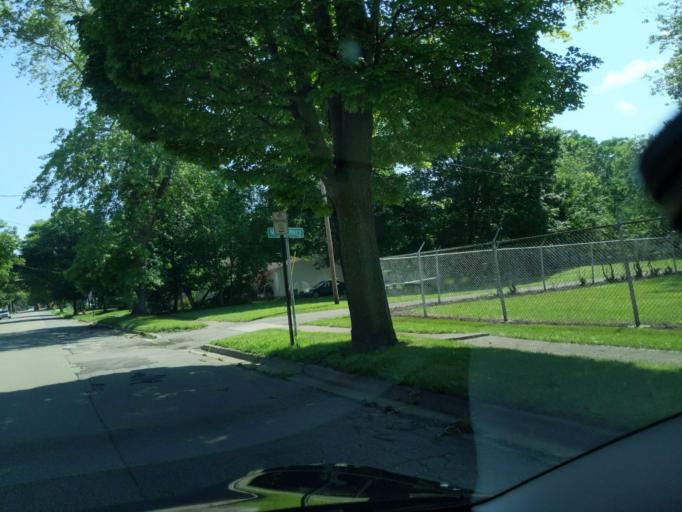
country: US
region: Michigan
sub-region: Jackson County
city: Jackson
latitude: 42.2577
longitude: -84.4119
